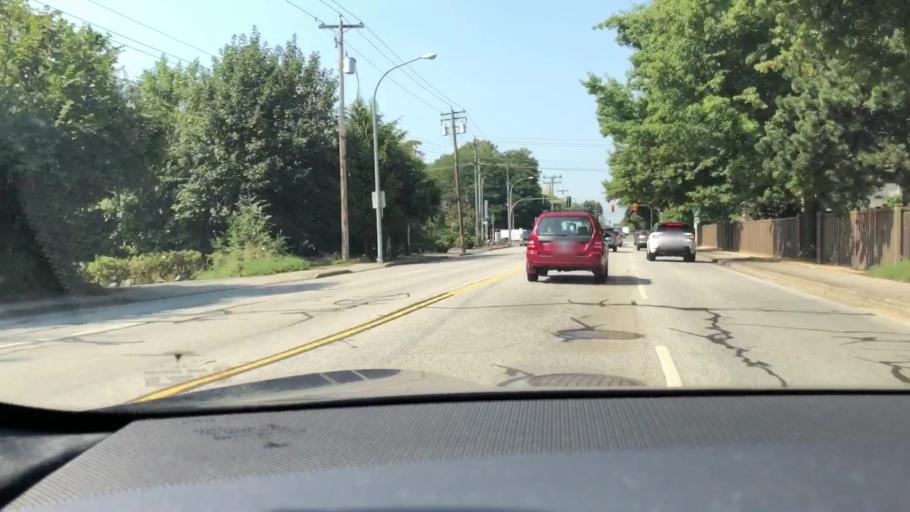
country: CA
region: British Columbia
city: Richmond
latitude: 49.1847
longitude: -123.1227
